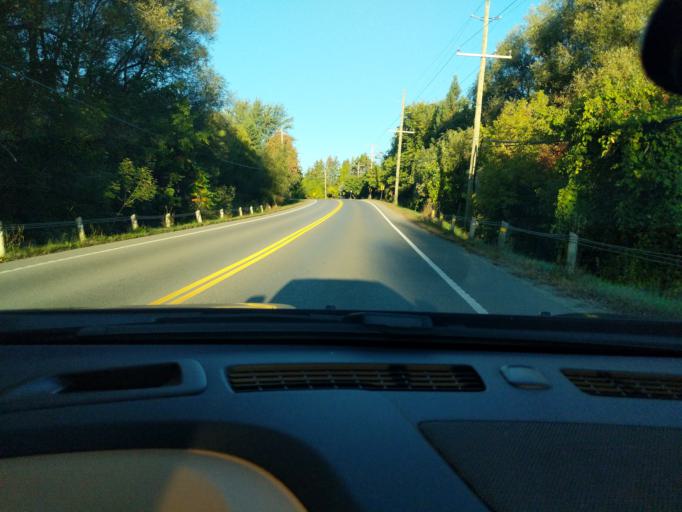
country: CA
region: Ontario
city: Collingwood
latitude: 44.4989
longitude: -80.2776
